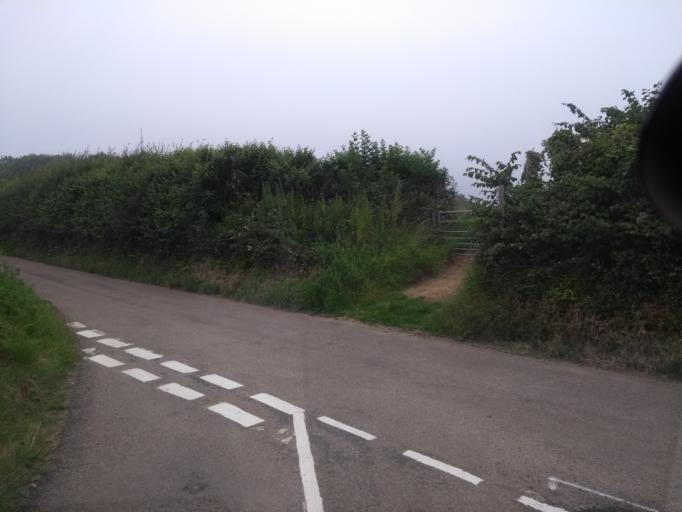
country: GB
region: England
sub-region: Dorset
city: Bridport
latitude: 50.7290
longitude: -2.7864
